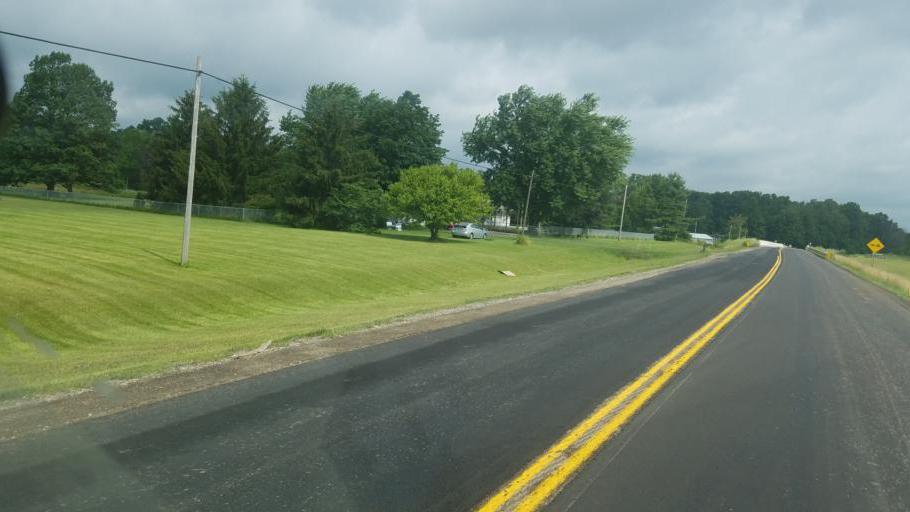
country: US
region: Ohio
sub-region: Knox County
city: Fredericktown
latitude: 40.5355
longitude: -82.6637
